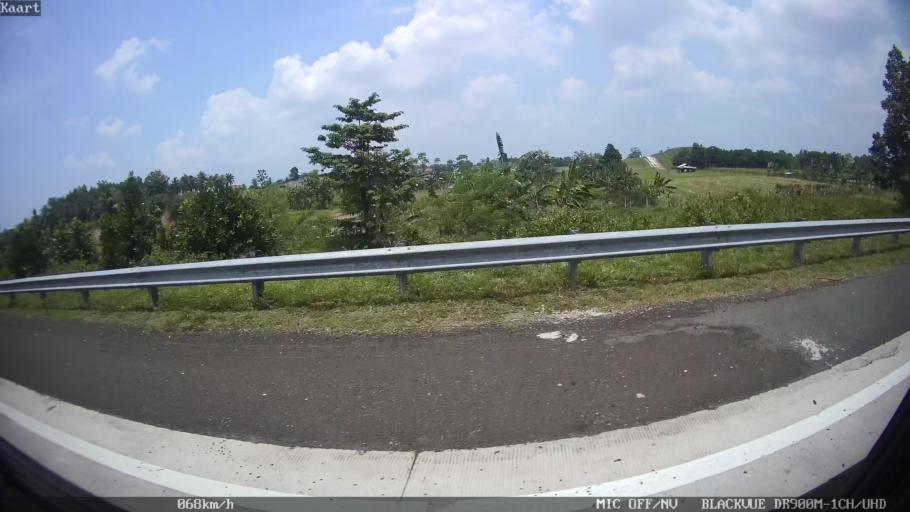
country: ID
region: Lampung
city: Natar
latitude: -5.2837
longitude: 105.2186
